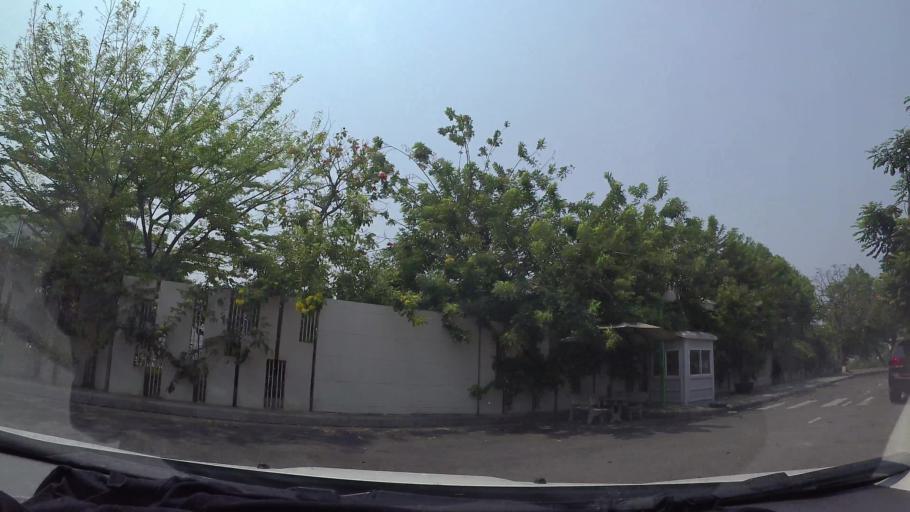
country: VN
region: Da Nang
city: Cam Le
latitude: 16.0122
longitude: 108.2089
